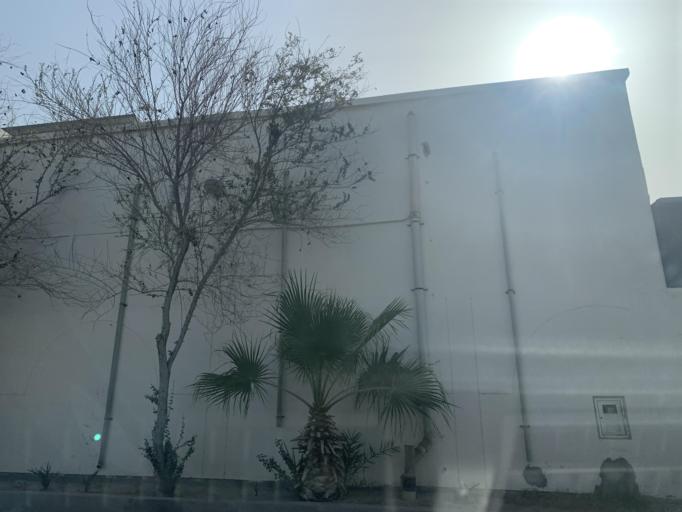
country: BH
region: Northern
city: Madinat `Isa
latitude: 26.1903
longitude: 50.5610
